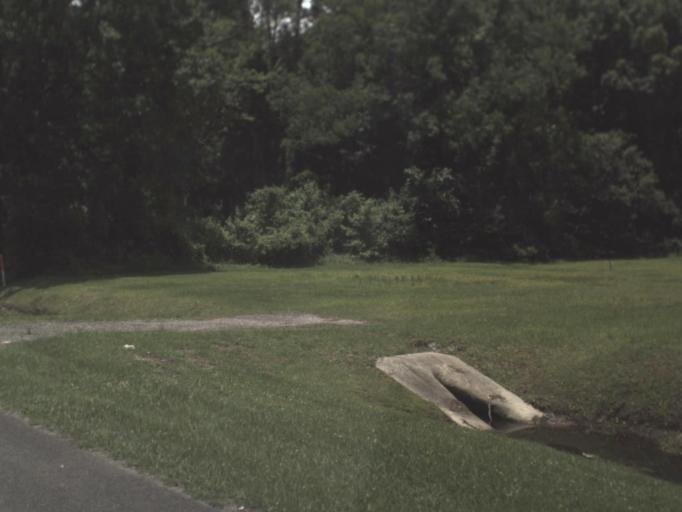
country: US
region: Florida
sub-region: Duval County
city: Jacksonville
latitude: 30.3893
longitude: -81.7348
